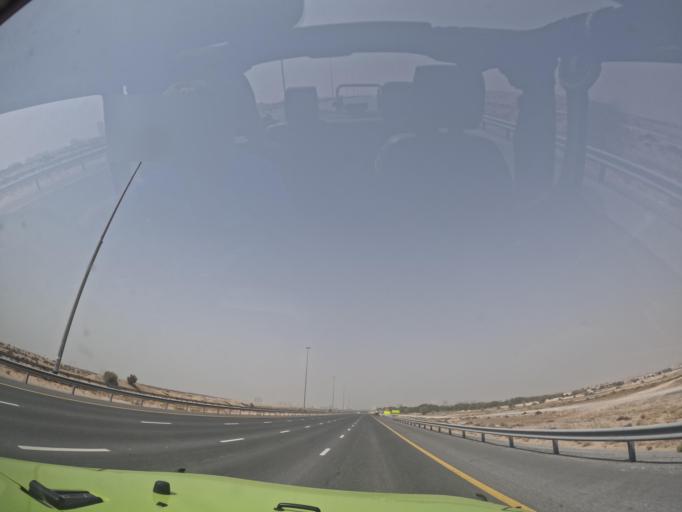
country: AE
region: Dubai
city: Dubai
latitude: 25.0795
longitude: 55.3382
